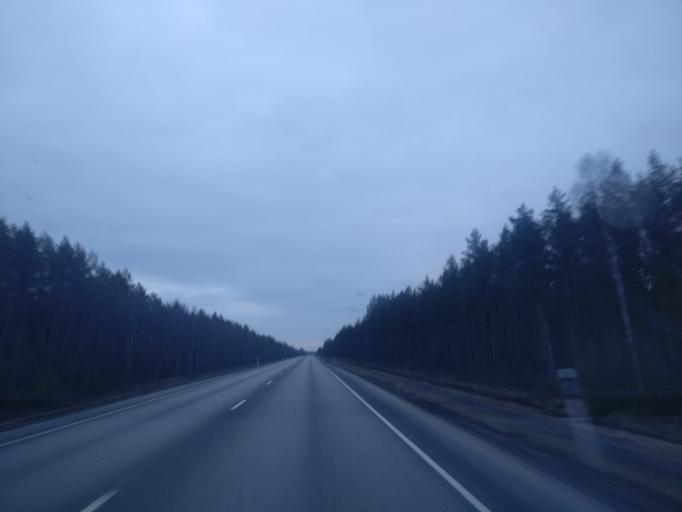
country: FI
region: Northern Ostrobothnia
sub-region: Haapavesi-Siikalatva
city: Rantsila
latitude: 64.5327
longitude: 25.6695
